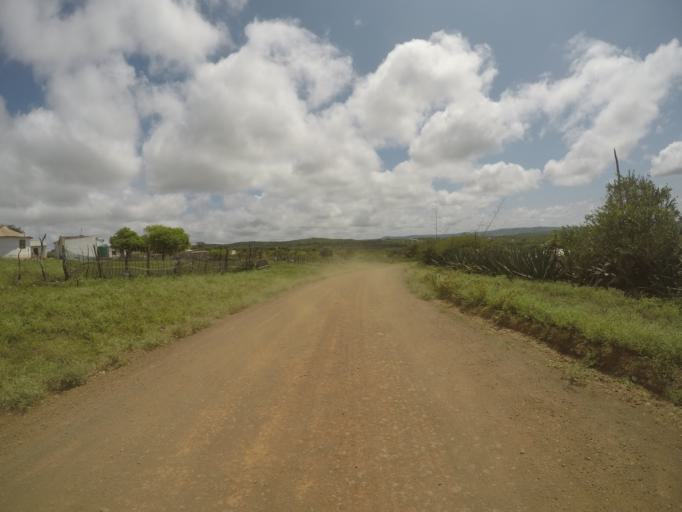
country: ZA
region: KwaZulu-Natal
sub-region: uThungulu District Municipality
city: Empangeni
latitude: -28.5756
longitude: 31.8379
